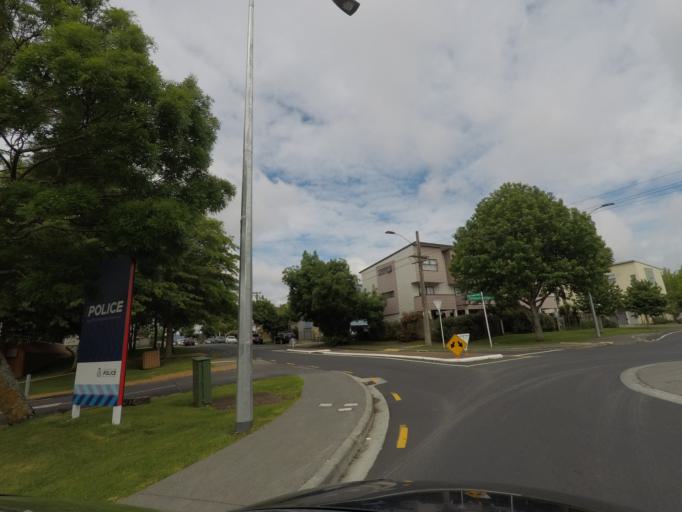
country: NZ
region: Auckland
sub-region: Auckland
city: Rosebank
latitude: -36.8740
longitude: 174.6293
